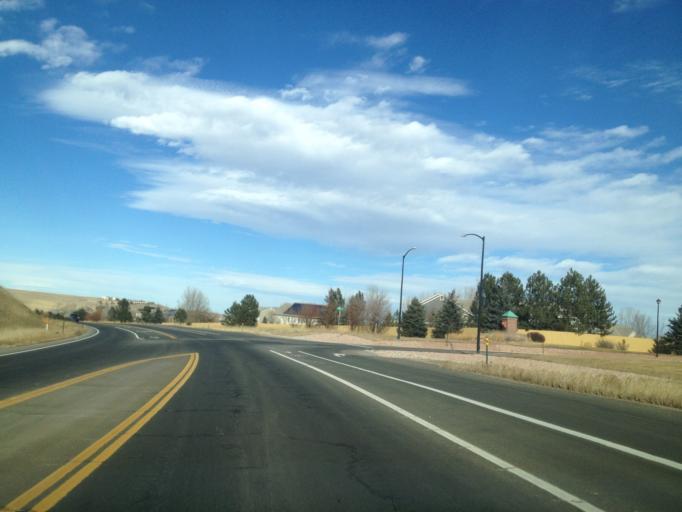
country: US
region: Colorado
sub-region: Boulder County
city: Superior
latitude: 39.9169
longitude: -105.1637
